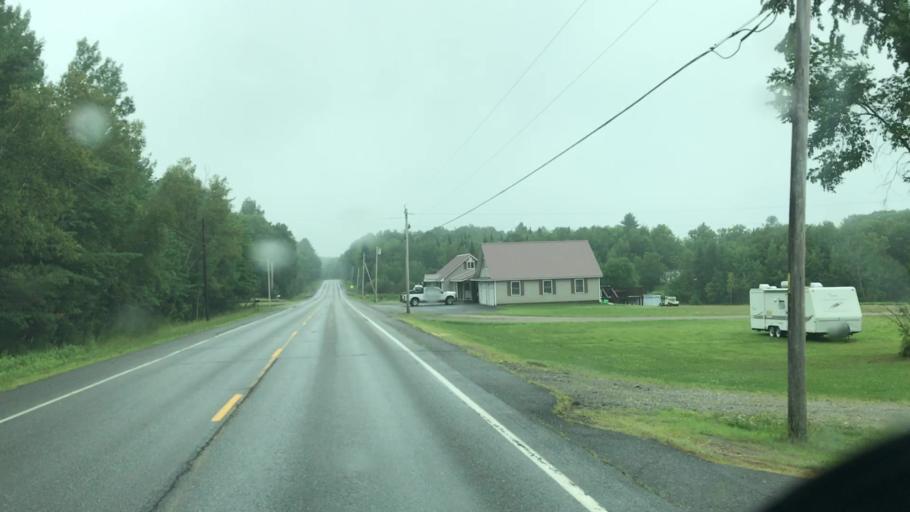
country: US
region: Maine
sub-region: Penobscot County
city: Howland
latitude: 45.2780
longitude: -68.6327
